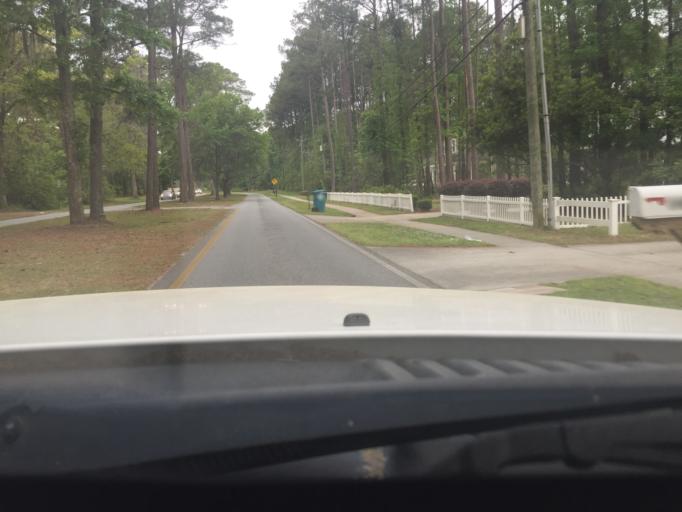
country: US
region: Georgia
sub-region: Chatham County
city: Georgetown
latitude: 31.9713
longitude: -81.2285
